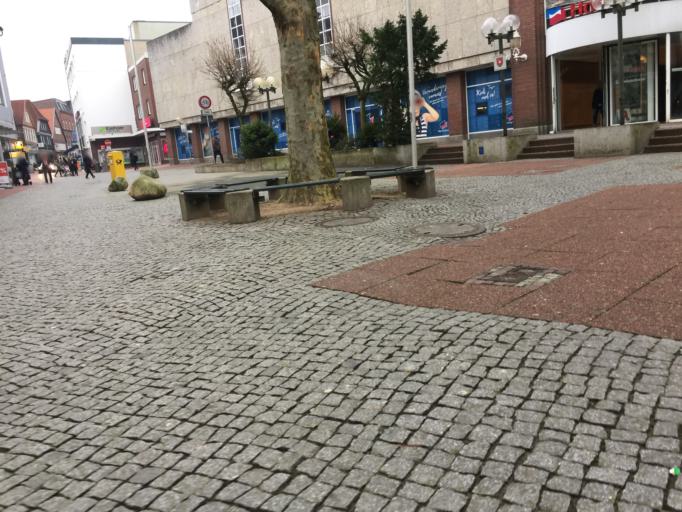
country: DE
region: Schleswig-Holstein
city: Itzehoe
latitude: 53.9251
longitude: 9.5166
